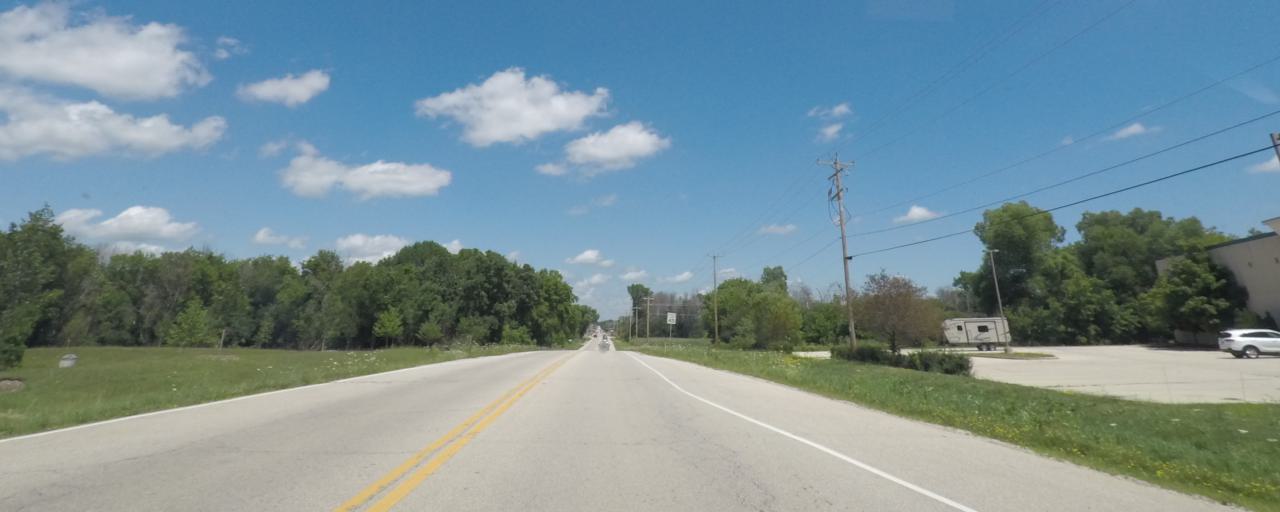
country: US
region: Wisconsin
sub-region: Waukesha County
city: Waukesha
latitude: 43.0437
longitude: -88.1859
